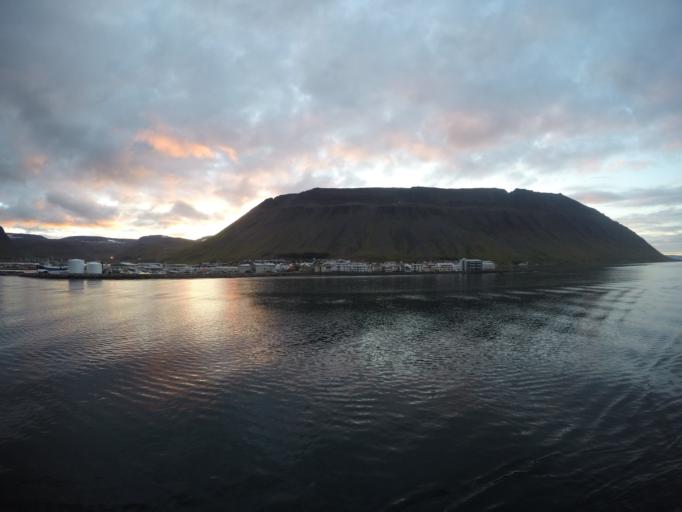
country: IS
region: Westfjords
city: Isafjoerdur
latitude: 66.0690
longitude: -23.1097
